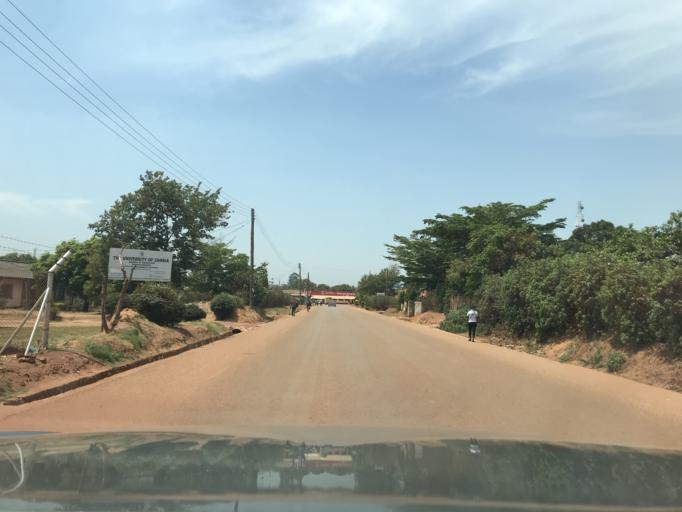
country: ZM
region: Northern
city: Kasama
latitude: -10.2038
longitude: 31.1849
